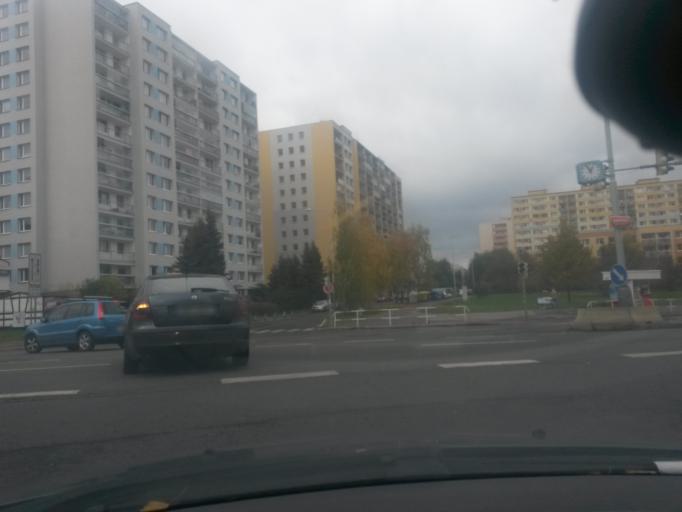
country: CZ
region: Central Bohemia
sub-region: Okres Praha-Zapad
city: Pruhonice
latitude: 50.0313
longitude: 14.5337
